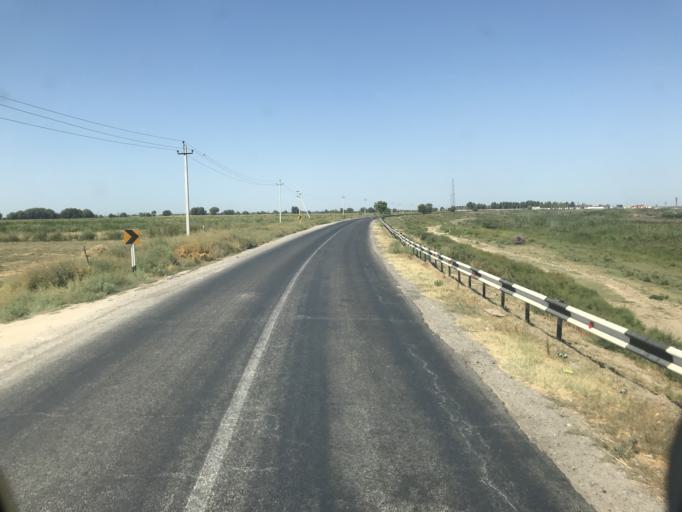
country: KZ
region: Ongtustik Qazaqstan
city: Ilyich
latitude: 40.9505
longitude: 68.4765
